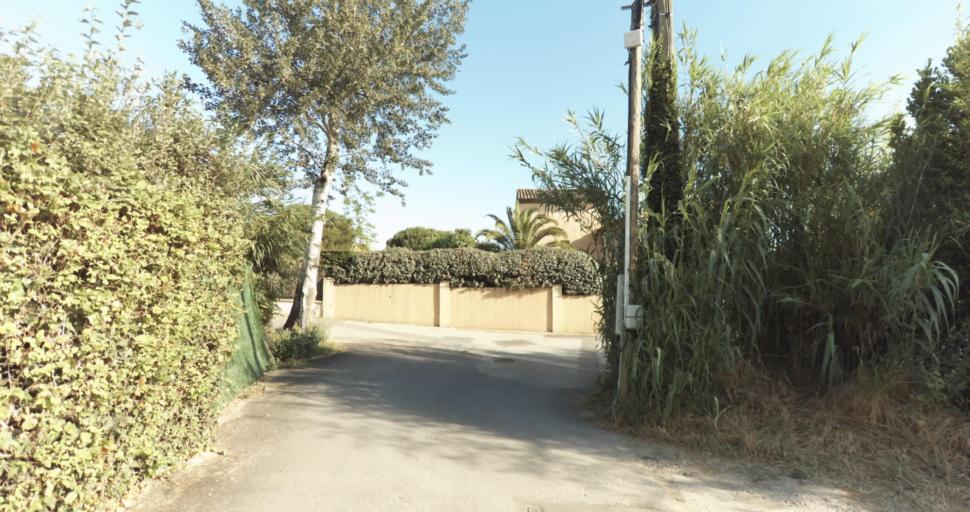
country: FR
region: Provence-Alpes-Cote d'Azur
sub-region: Departement du Var
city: Saint-Tropez
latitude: 43.2592
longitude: 6.6292
